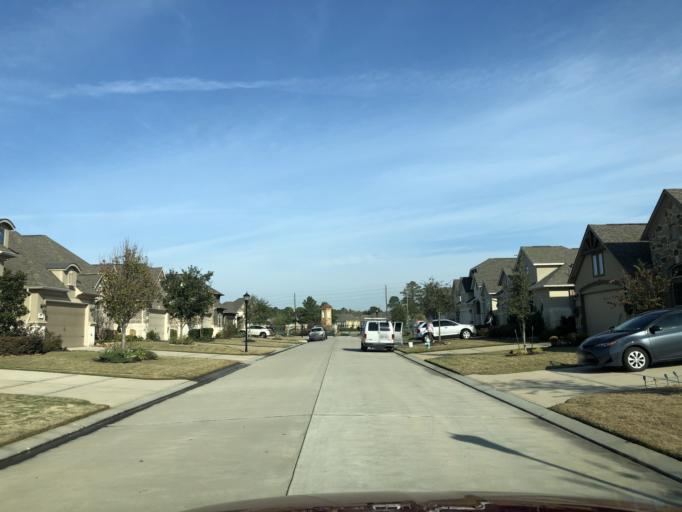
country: US
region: Texas
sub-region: Harris County
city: Tomball
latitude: 30.0331
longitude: -95.5577
